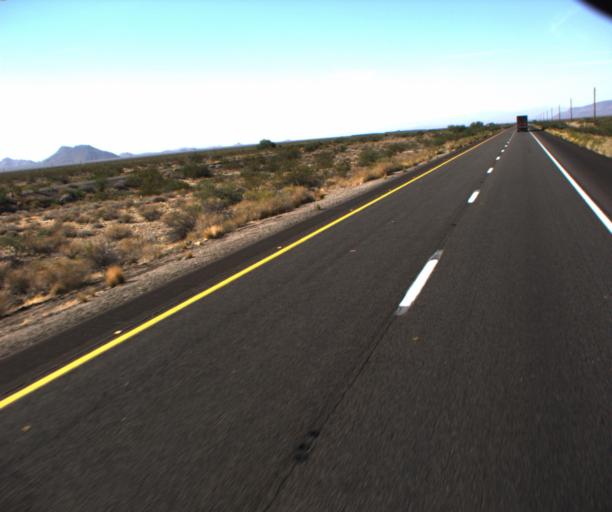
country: US
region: Arizona
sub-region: Mohave County
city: Kingman
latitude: 35.0060
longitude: -114.1360
